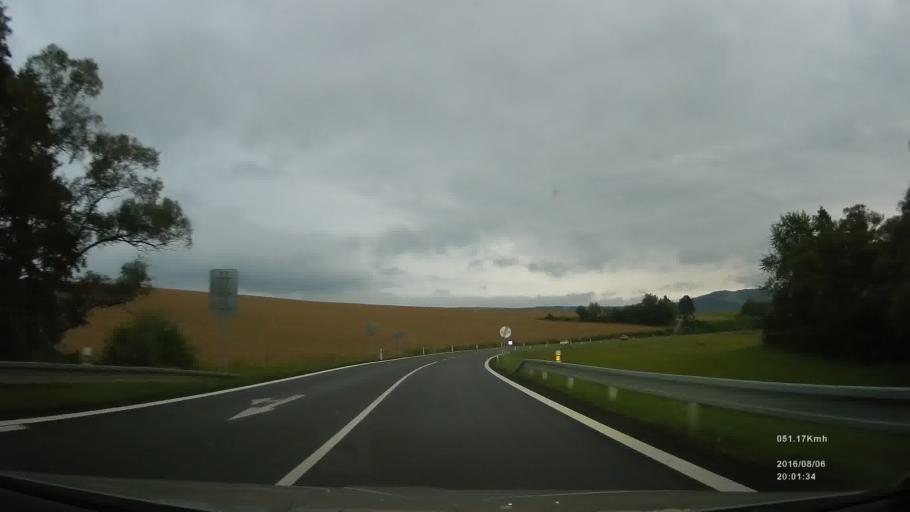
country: SK
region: Presovsky
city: Svidnik
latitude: 49.2454
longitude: 21.5866
